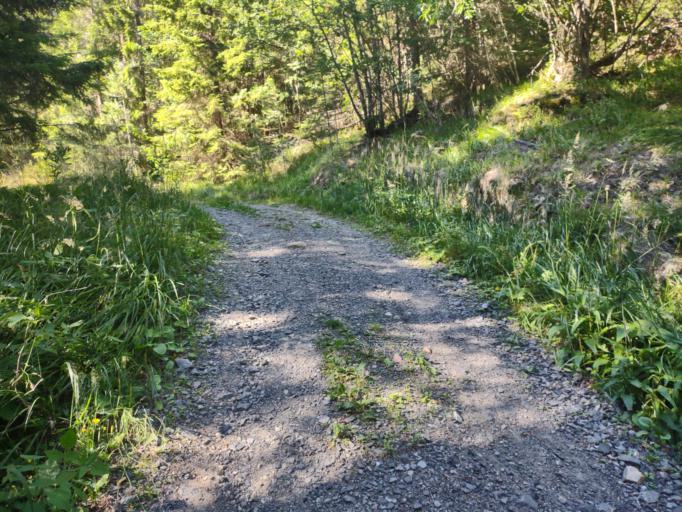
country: NO
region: Akershus
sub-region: Raelingen
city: Fjerdingby
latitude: 59.8847
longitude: 11.0420
